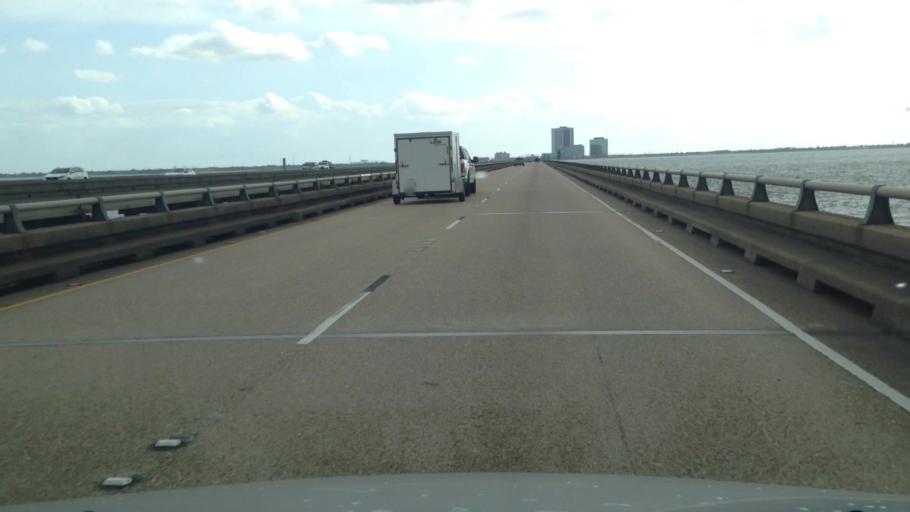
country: US
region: Louisiana
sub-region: Jefferson Parish
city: Metairie
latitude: 30.0503
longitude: -90.1491
